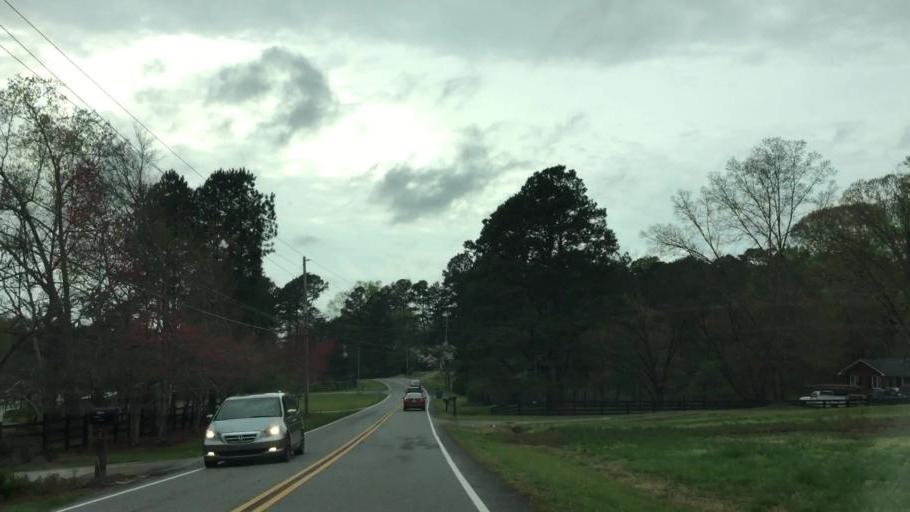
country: US
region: Georgia
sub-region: Fulton County
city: Milton
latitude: 34.1996
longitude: -84.3806
